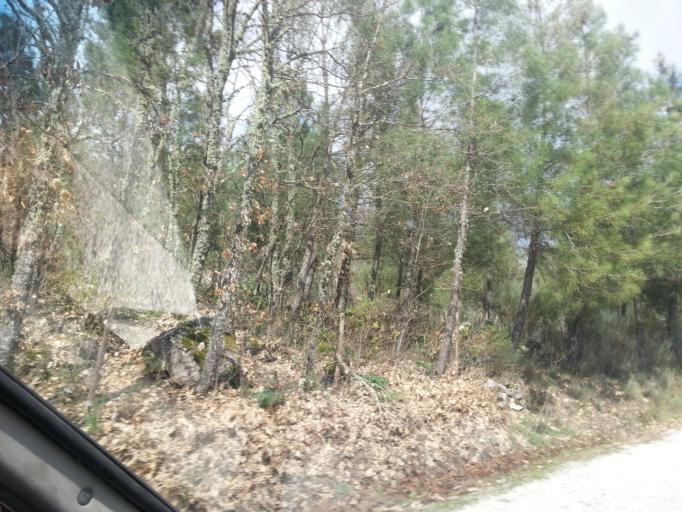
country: PT
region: Guarda
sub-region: Fornos de Algodres
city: Fornos de Algodres
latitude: 40.6494
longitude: -7.5029
